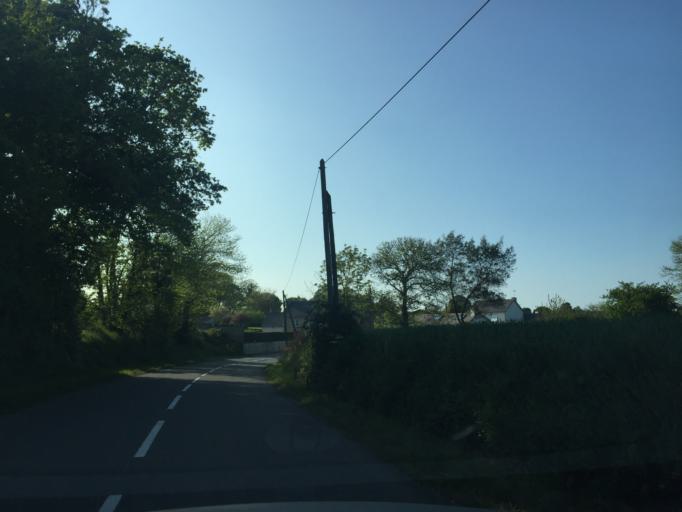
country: FR
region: Brittany
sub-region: Departement des Cotes-d'Armor
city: Saint-Cast-le-Guildo
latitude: 48.6064
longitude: -2.2540
